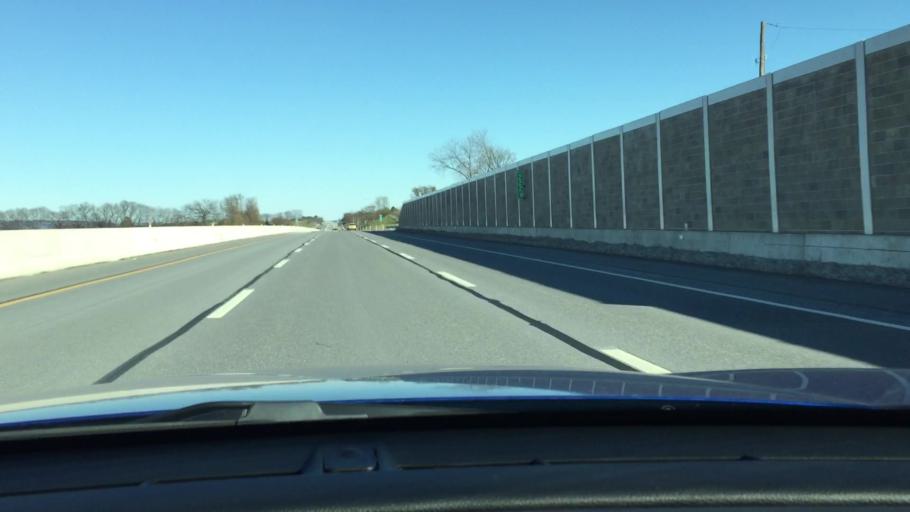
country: US
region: Pennsylvania
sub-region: Cumberland County
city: Carlisle
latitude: 40.2127
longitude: -77.2174
